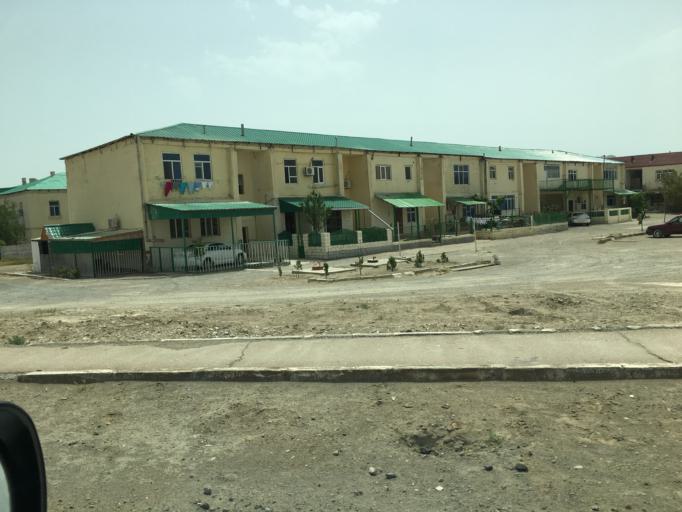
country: TM
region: Balkan
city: Turkmenbasy
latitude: 40.0136
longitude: 53.1092
